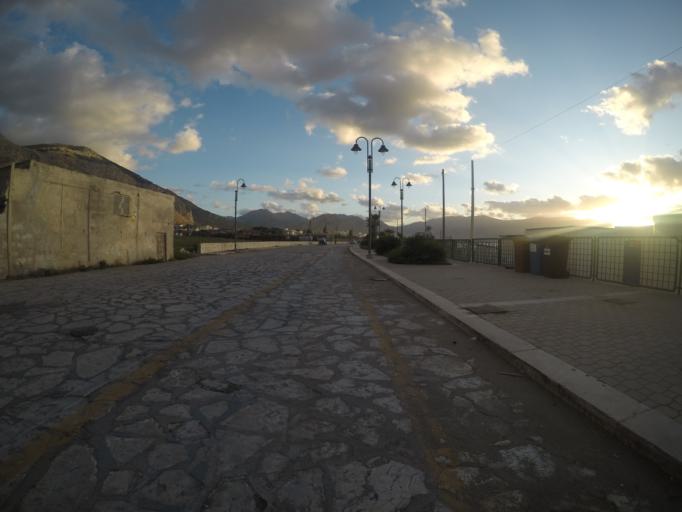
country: IT
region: Sicily
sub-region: Palermo
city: Isola delle Femmine
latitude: 38.1915
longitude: 13.2436
